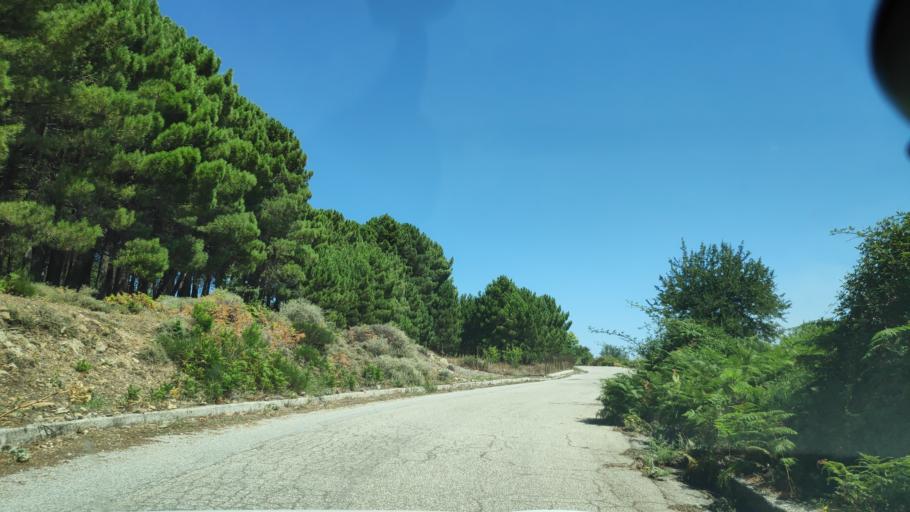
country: IT
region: Calabria
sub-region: Provincia di Reggio Calabria
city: Bova
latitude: 38.0270
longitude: 15.9412
